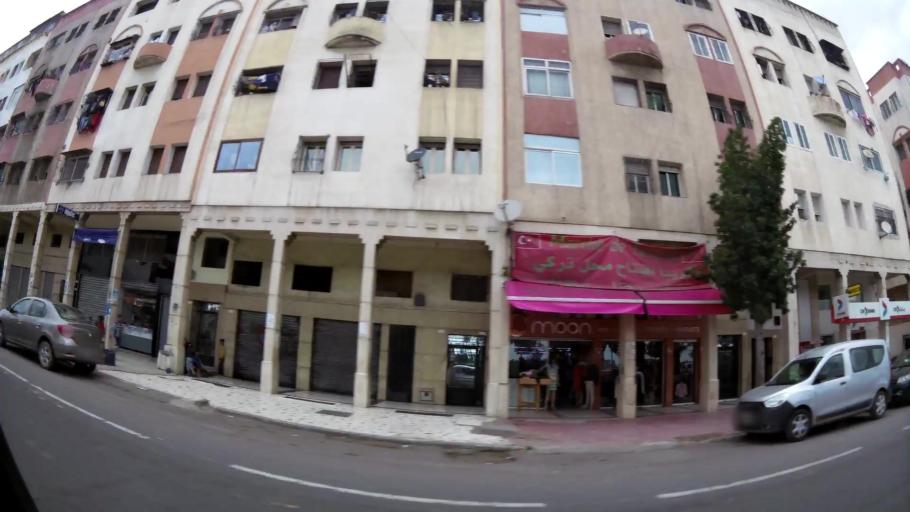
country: MA
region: Grand Casablanca
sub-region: Mediouna
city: Tit Mellil
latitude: 33.5678
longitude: -7.5398
